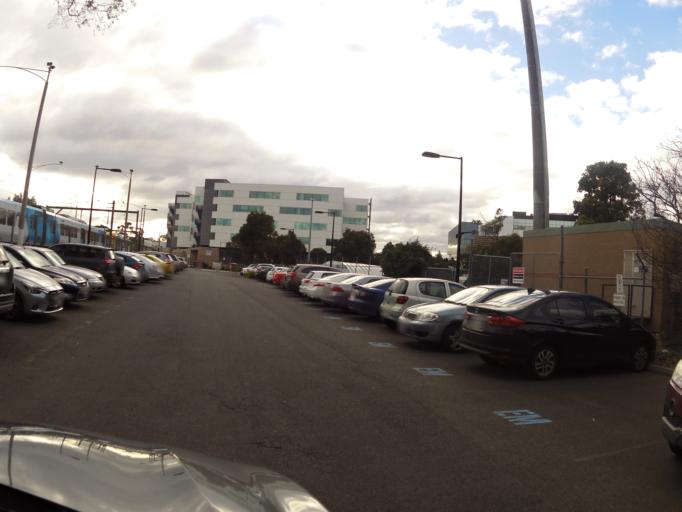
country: AU
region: Victoria
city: Toorak
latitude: -37.8292
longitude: 145.0204
